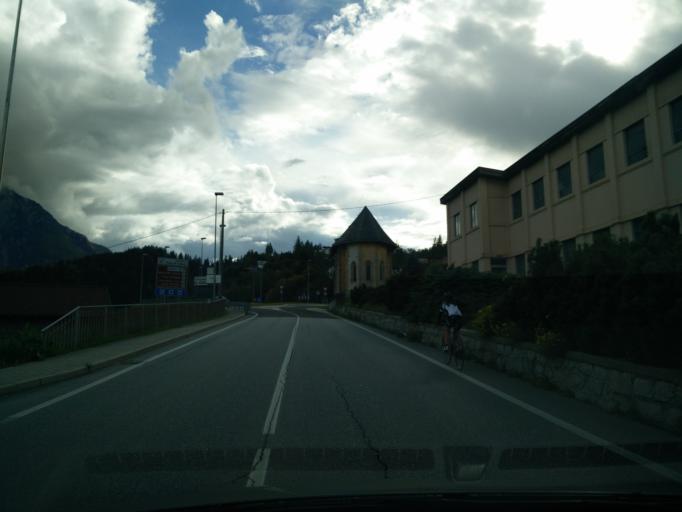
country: IT
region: Veneto
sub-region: Provincia di Belluno
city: Calalzo di Cadore
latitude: 46.4375
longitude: 12.3798
